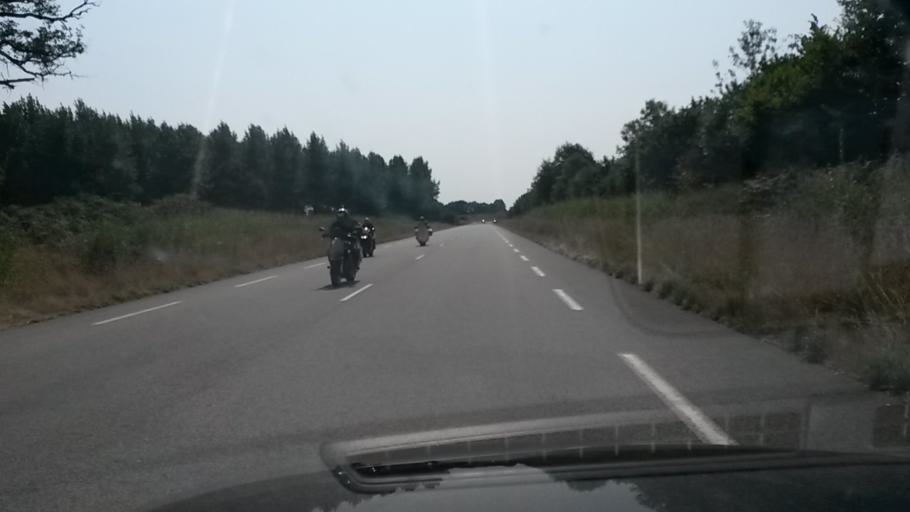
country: FR
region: Pays de la Loire
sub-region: Departement de la Mayenne
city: Chemaze
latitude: 47.7888
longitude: -0.7633
